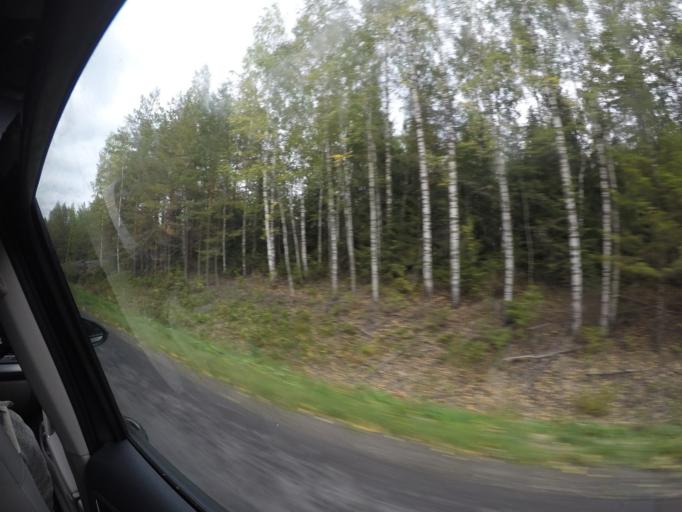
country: FI
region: Haeme
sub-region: Haemeenlinna
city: Parola
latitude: 61.1694
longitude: 24.4112
